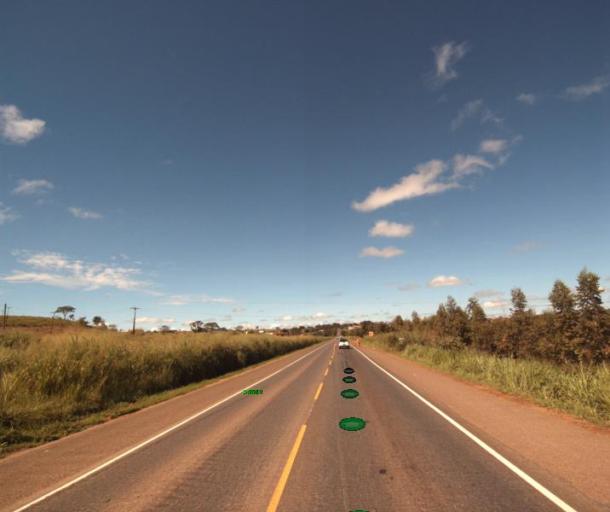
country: BR
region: Goias
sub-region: Rialma
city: Rialma
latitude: -15.2990
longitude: -49.5698
